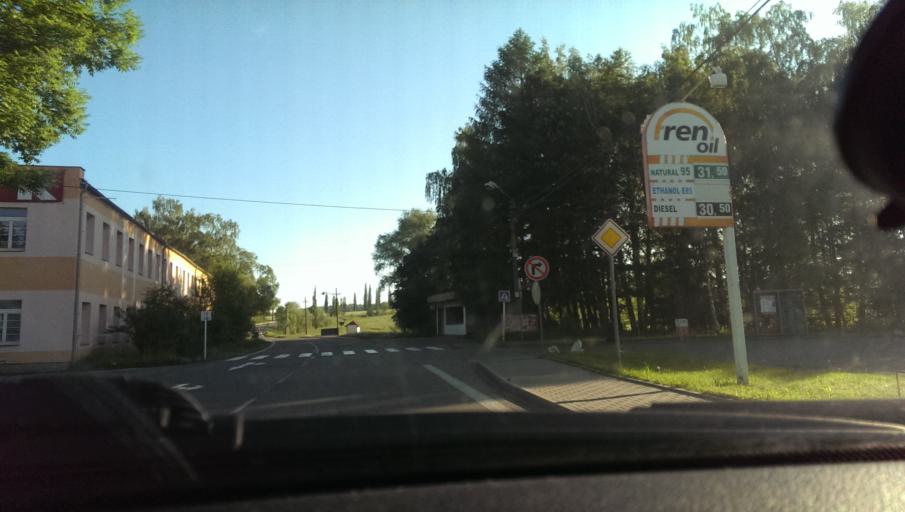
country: CZ
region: Moravskoslezsky
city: Frenstat pod Radhostem
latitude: 49.5516
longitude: 18.2163
